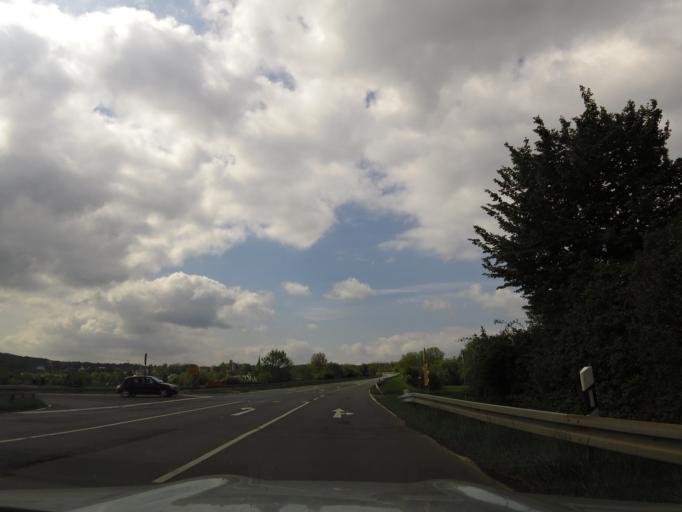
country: DE
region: Hesse
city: Burgsolms
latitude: 50.5486
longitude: 8.4102
